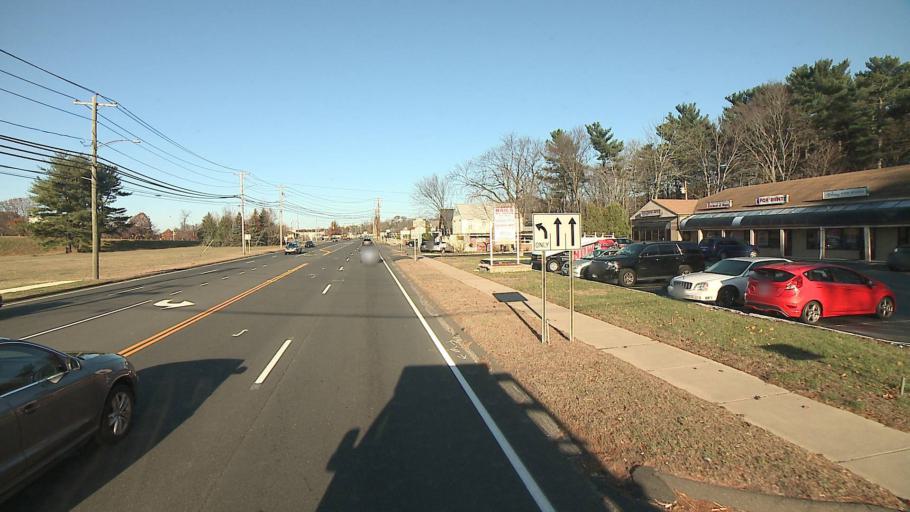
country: US
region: Connecticut
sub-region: New Haven County
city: North Haven
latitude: 41.4088
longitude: -72.8439
